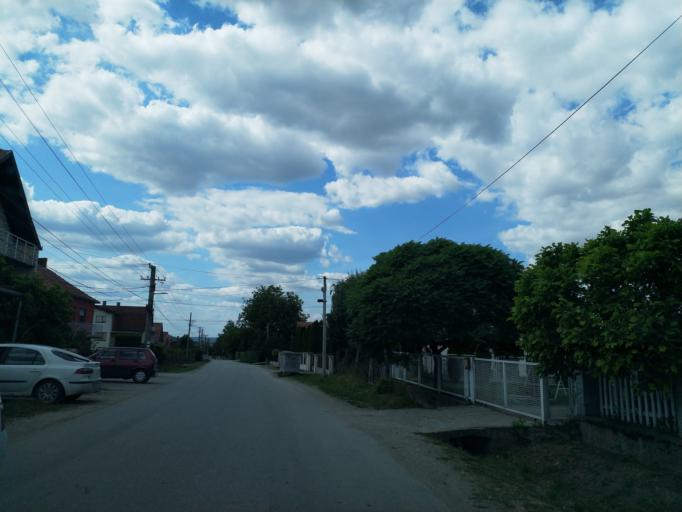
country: RS
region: Central Serbia
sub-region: Pomoravski Okrug
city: Jagodina
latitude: 43.9493
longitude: 21.2942
